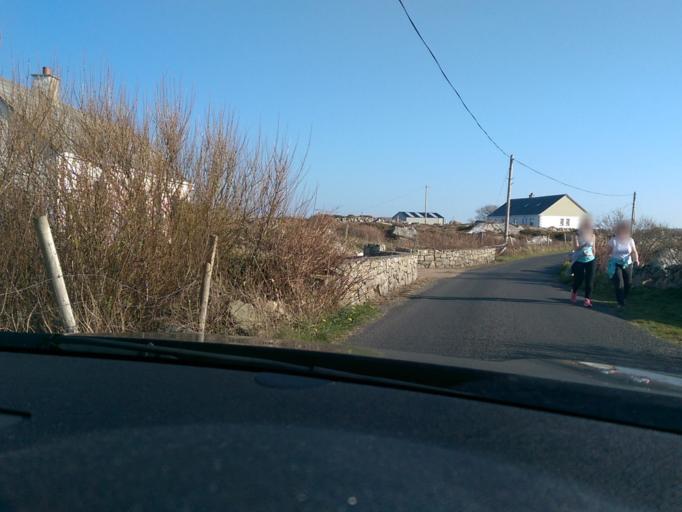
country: IE
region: Connaught
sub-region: County Galway
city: Clifden
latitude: 53.3586
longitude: -9.8762
